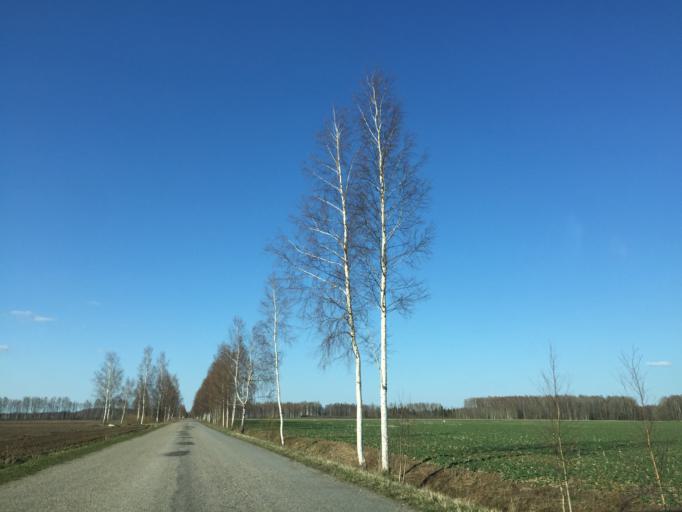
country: EE
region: Valgamaa
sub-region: Torva linn
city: Torva
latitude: 58.2381
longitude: 25.9453
